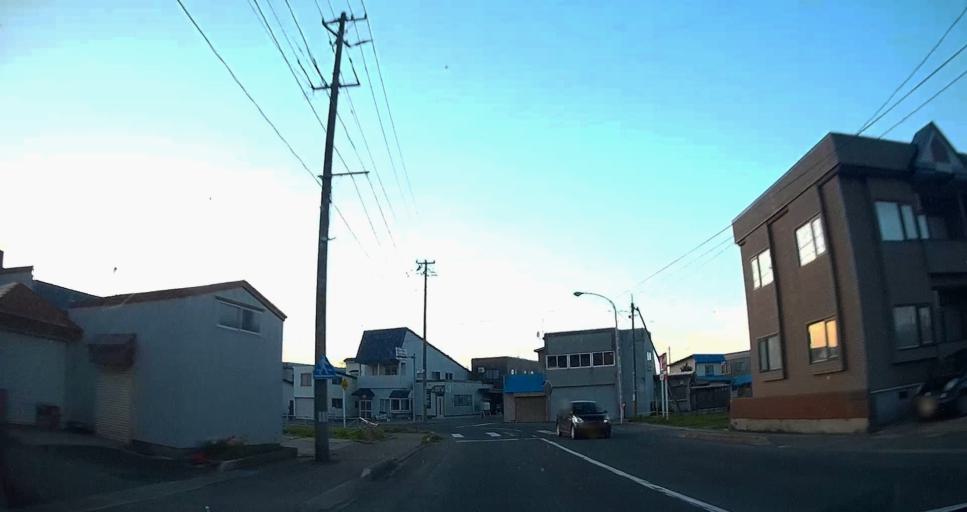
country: JP
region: Aomori
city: Misawa
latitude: 40.8680
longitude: 141.1226
